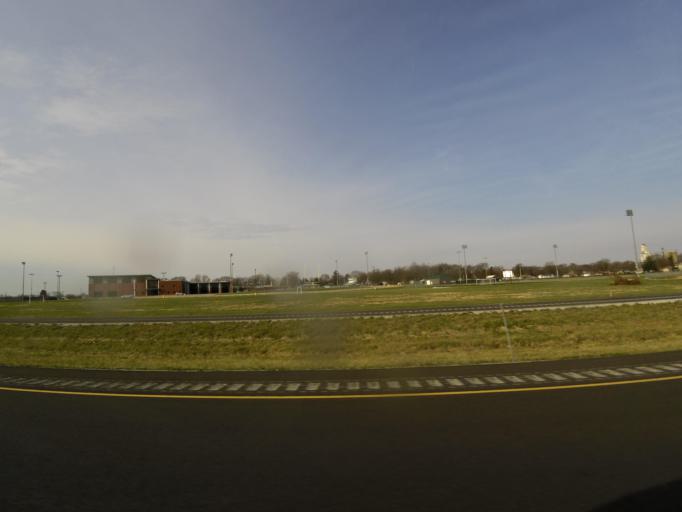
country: US
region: Illinois
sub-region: Macon County
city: Macon
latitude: 39.7029
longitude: -88.9928
